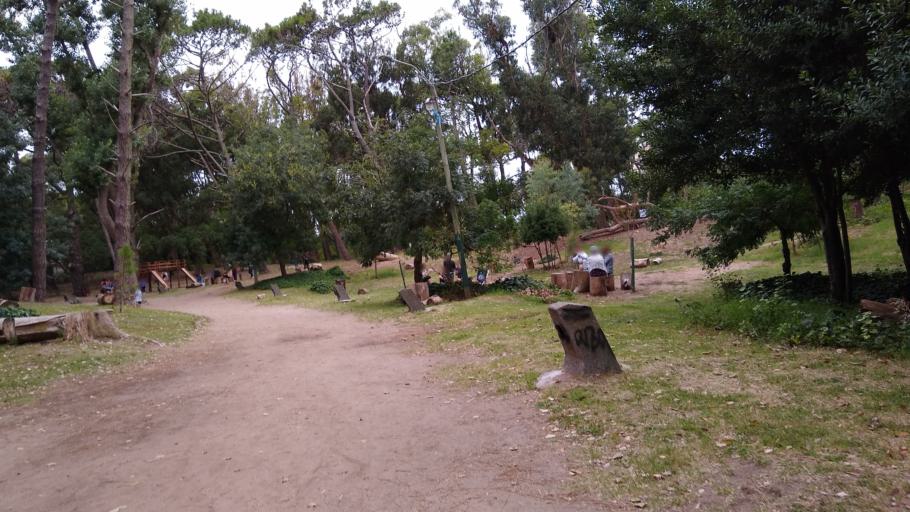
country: AR
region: Buenos Aires
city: Villa Gesell
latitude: -37.2523
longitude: -56.9638
